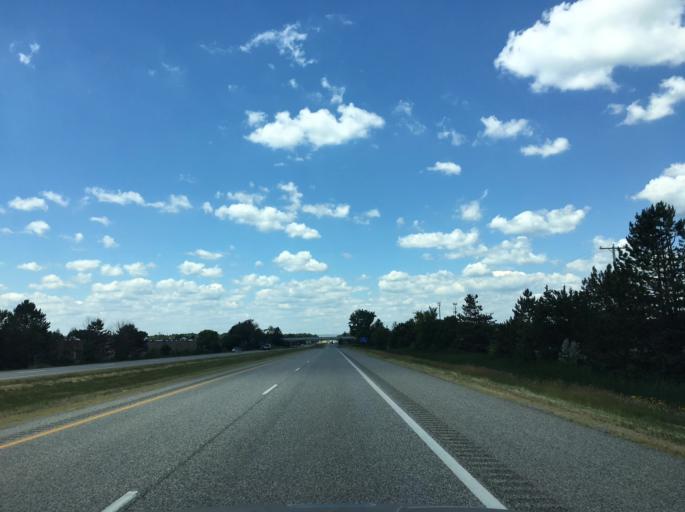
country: US
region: Michigan
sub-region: Midland County
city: Midland
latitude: 43.6560
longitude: -84.2215
